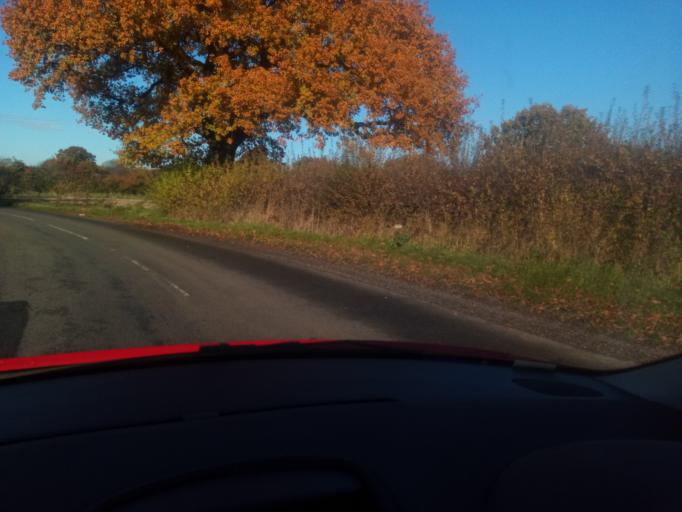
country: GB
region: England
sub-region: Derbyshire
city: Melbourne
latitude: 52.8543
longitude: -1.4349
